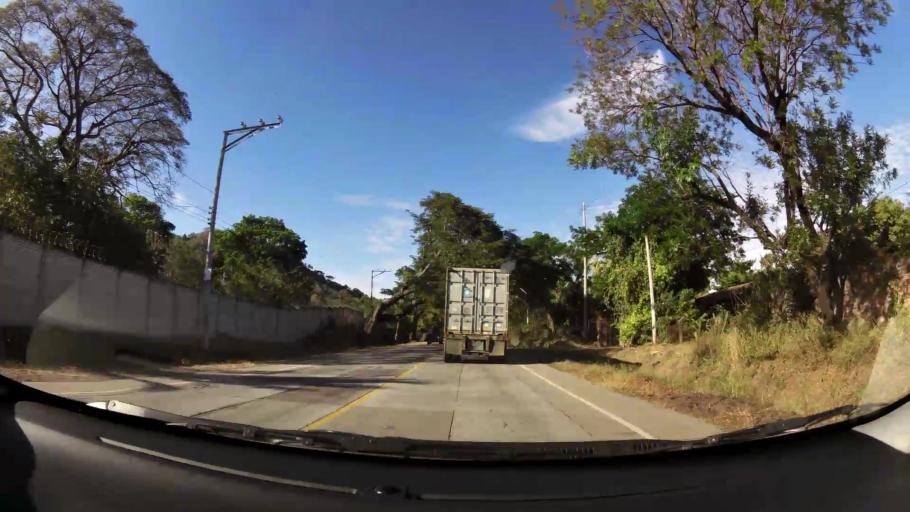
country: SV
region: Santa Ana
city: Texistepeque
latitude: 14.0856
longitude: -89.5000
